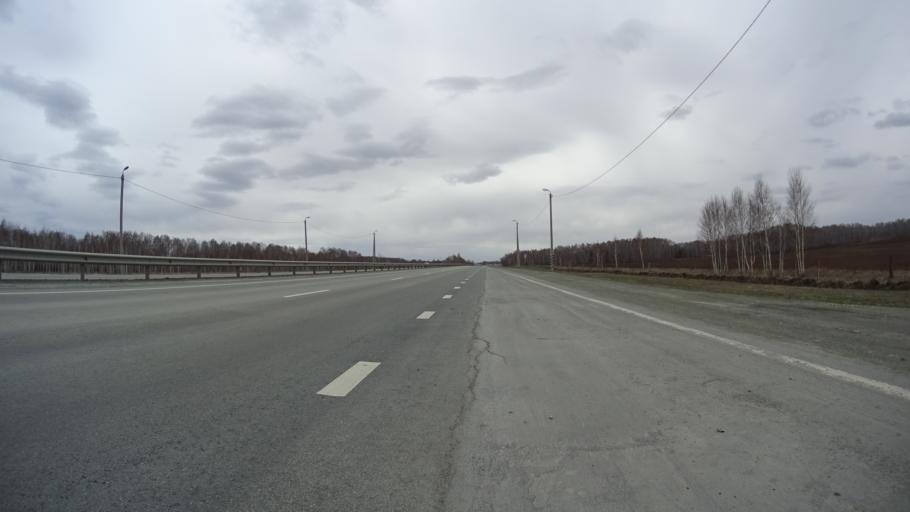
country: RU
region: Chelyabinsk
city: Yemanzhelinka
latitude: 54.8321
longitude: 61.3119
